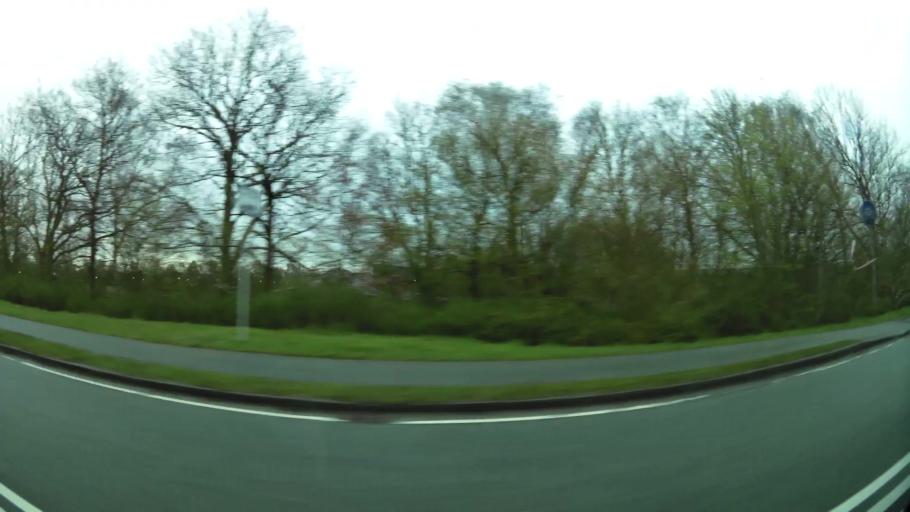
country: DK
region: Central Jutland
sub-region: Herning Kommune
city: Snejbjerg
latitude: 56.1305
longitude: 8.8844
